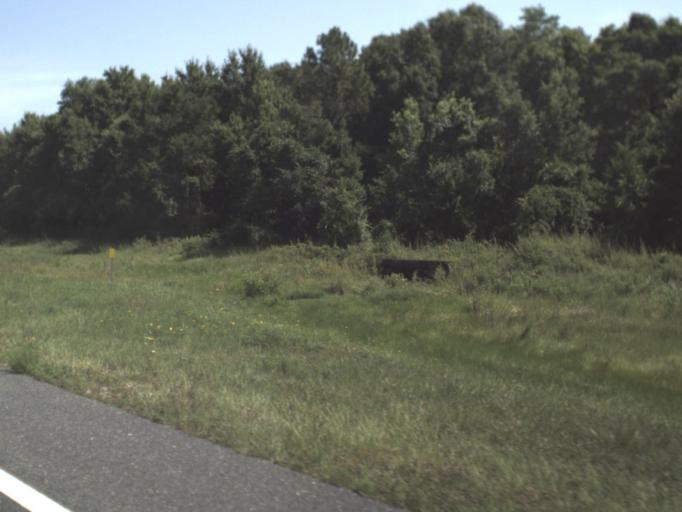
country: US
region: Florida
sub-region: Levy County
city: Chiefland
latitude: 29.4128
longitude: -82.8206
